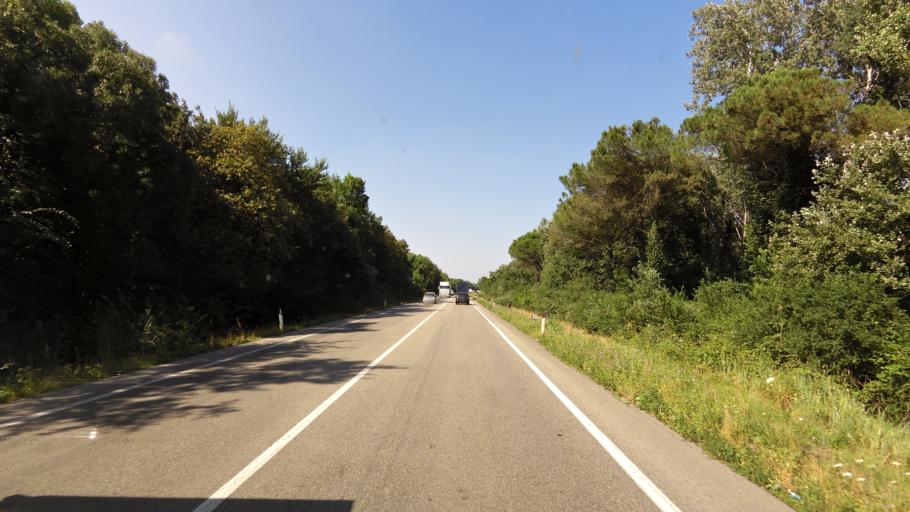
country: IT
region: Emilia-Romagna
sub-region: Provincia di Ravenna
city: Marina Romea
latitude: 44.4949
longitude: 12.2162
